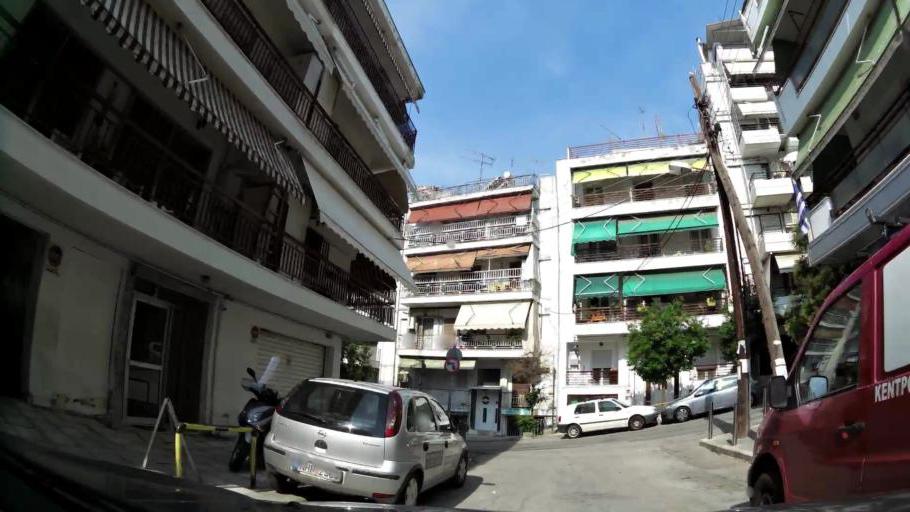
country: GR
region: Central Macedonia
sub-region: Nomos Thessalonikis
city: Sykies
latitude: 40.6516
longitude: 22.9517
